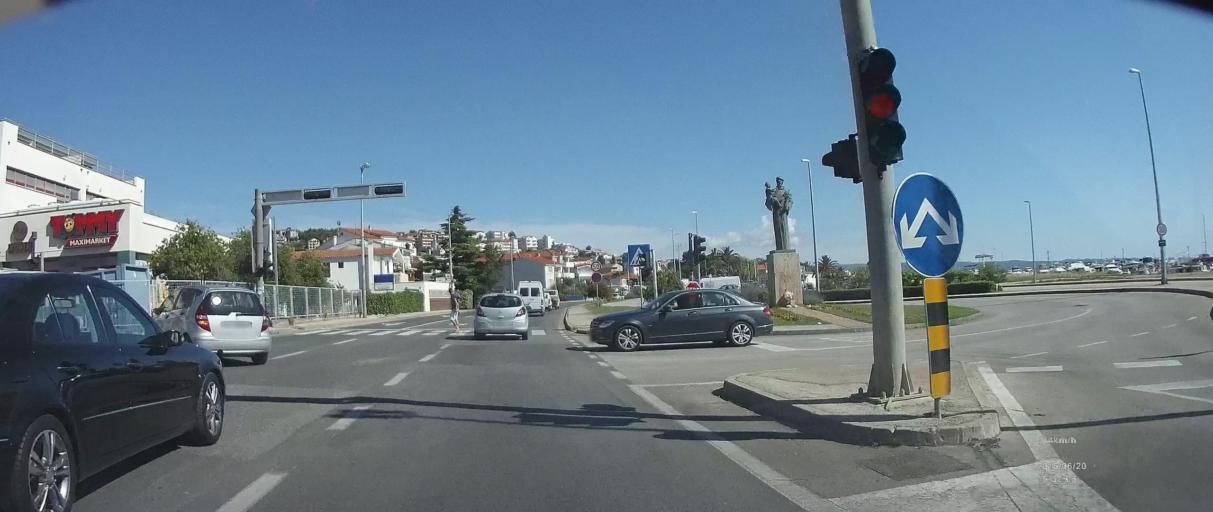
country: HR
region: Splitsko-Dalmatinska
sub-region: Grad Split
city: Stobrec
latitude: 43.5033
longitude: 16.5339
